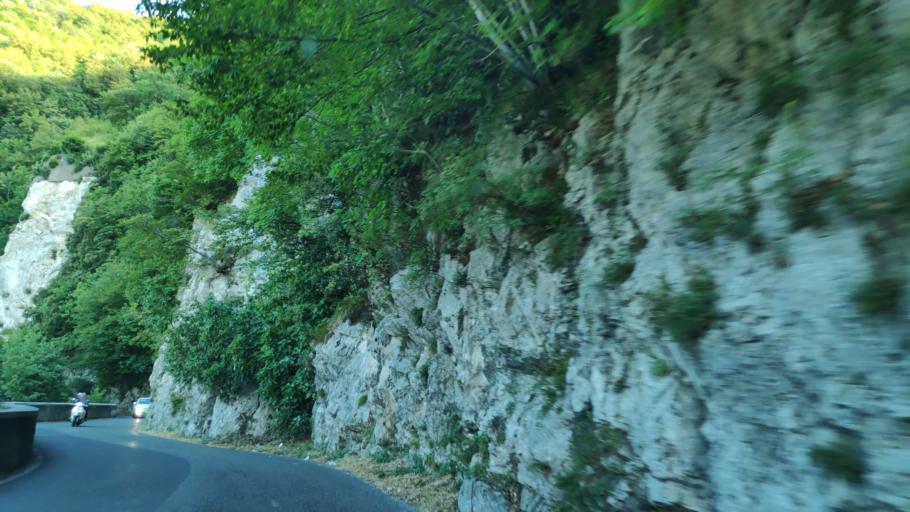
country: IT
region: Campania
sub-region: Provincia di Salerno
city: Corbara
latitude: 40.7188
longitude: 14.6113
